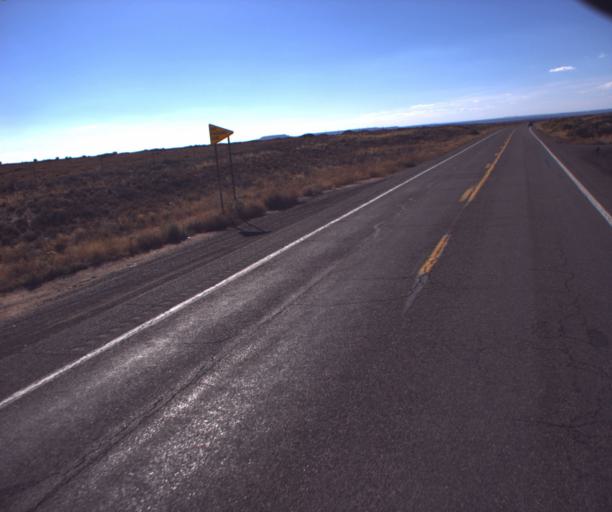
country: US
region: Arizona
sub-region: Coconino County
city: Kaibito
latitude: 36.6123
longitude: -111.0126
